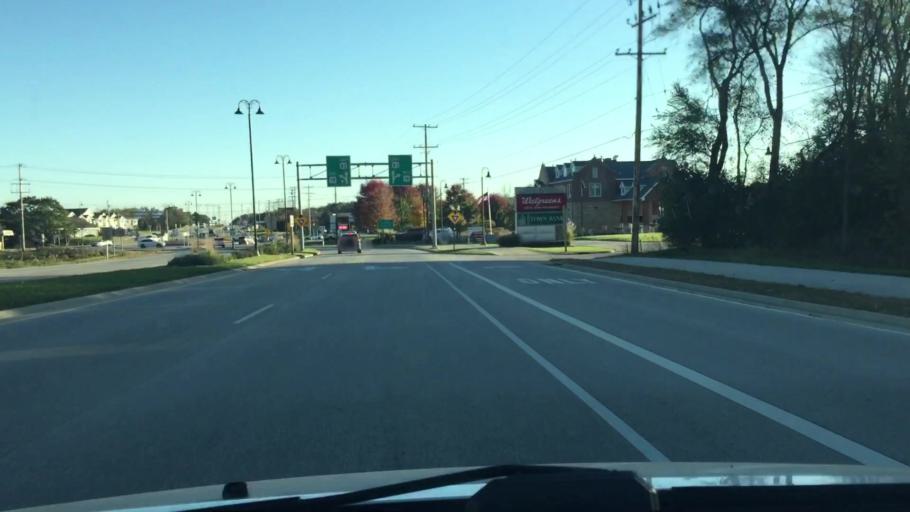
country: US
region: Wisconsin
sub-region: Waukesha County
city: Wales
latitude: 43.0137
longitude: -88.3840
